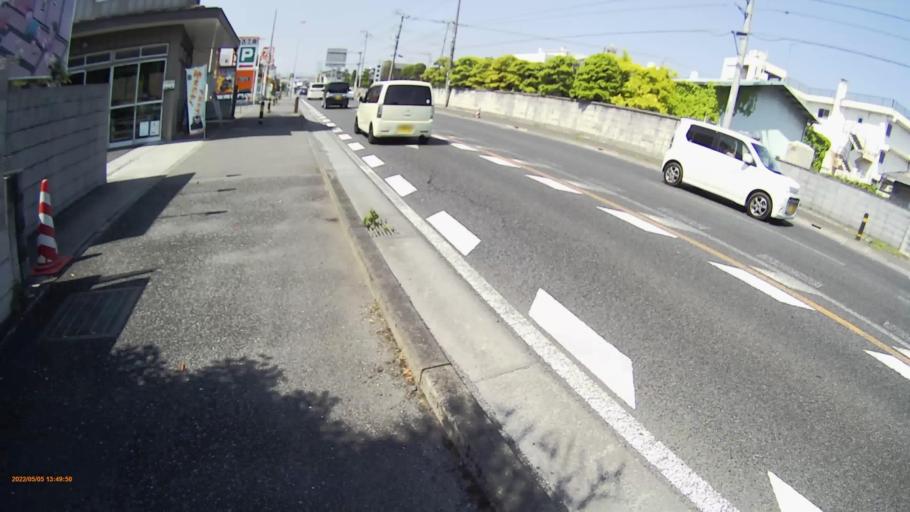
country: JP
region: Saitama
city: Kasukabe
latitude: 35.9926
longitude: 139.7524
